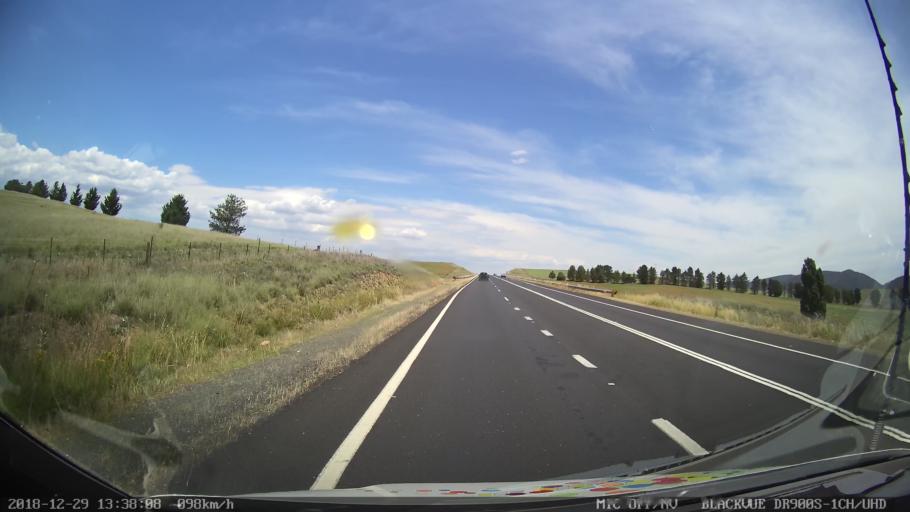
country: AU
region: New South Wales
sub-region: Cooma-Monaro
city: Cooma
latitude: -35.9943
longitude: 149.1400
